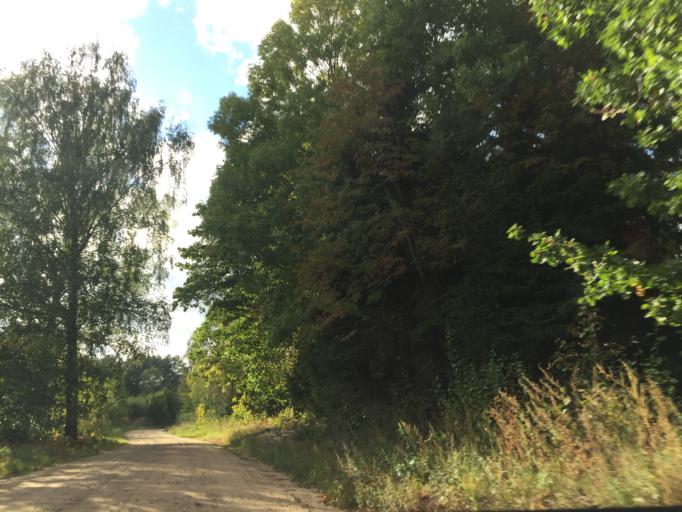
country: LV
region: Ligatne
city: Ligatne
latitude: 57.1311
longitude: 25.1071
